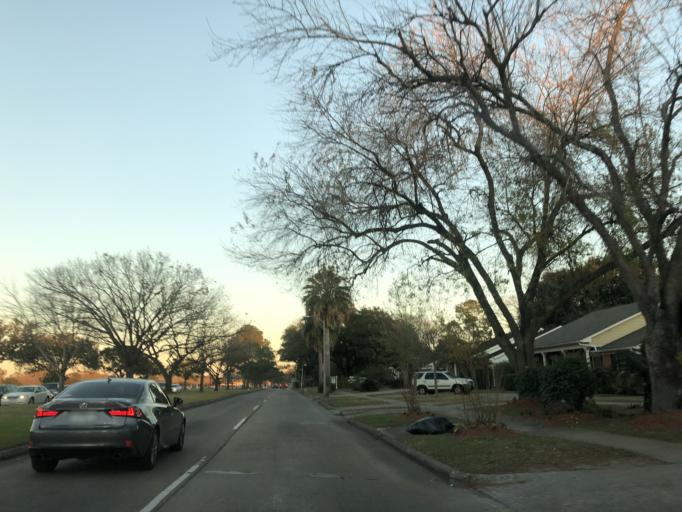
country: US
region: Texas
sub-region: Harris County
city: Bellaire
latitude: 29.6774
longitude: -95.4991
